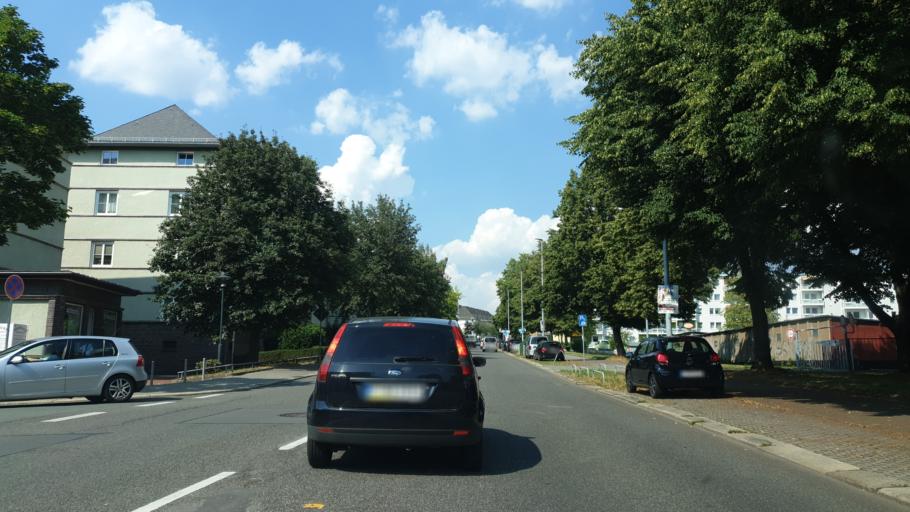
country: DE
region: Saxony
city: Hilbersdorf
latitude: 50.8328
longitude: 12.9544
